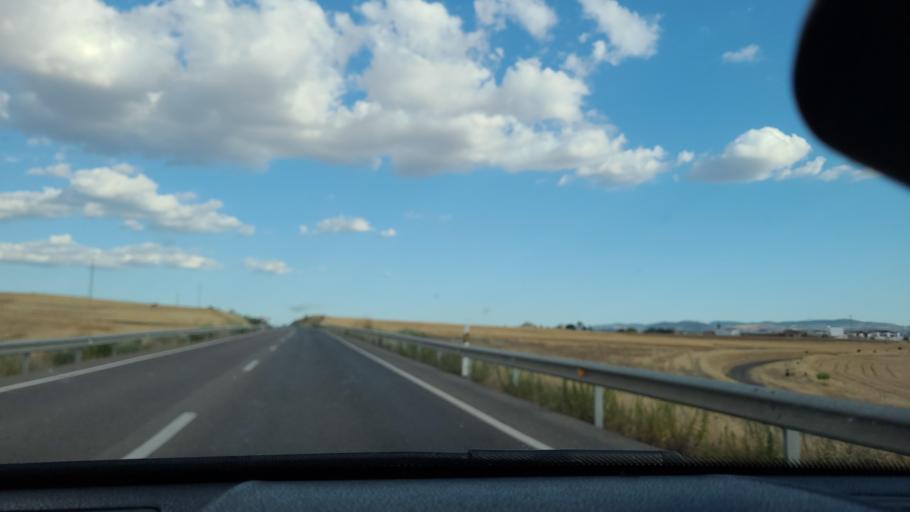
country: ES
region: Andalusia
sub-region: Province of Cordoba
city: Belmez
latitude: 38.2813
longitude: -5.2091
